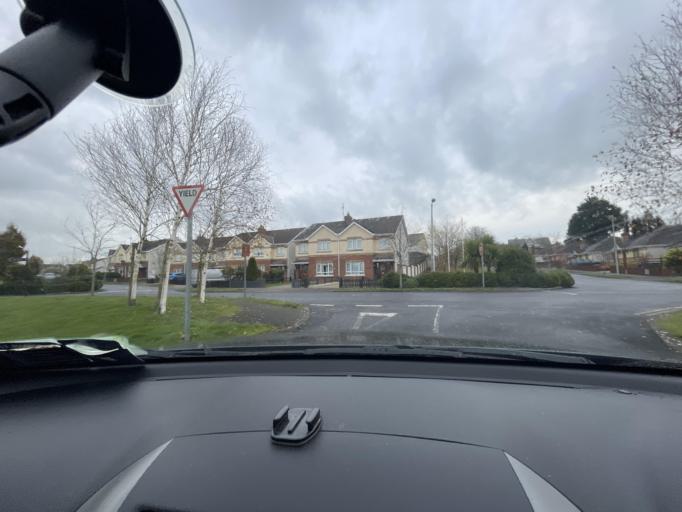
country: IE
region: Ulster
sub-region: An Cabhan
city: Virginia
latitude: 53.8367
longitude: -7.0766
